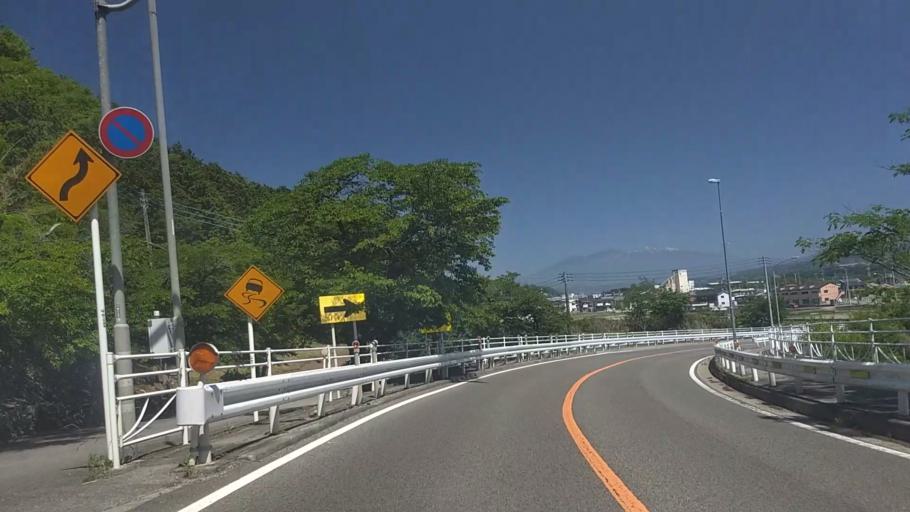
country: JP
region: Yamanashi
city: Nirasaki
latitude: 35.6858
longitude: 138.4615
